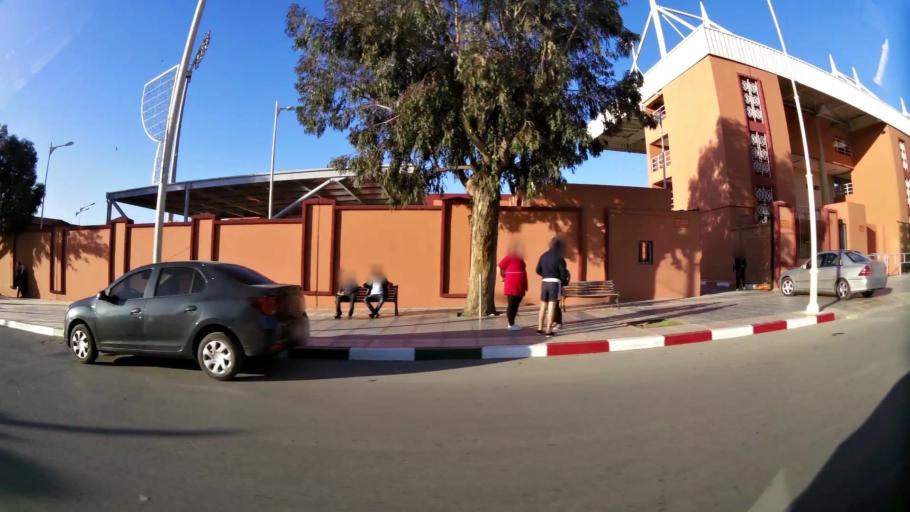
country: MA
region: Oriental
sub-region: Berkane-Taourirt
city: Berkane
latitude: 34.9267
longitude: -2.3267
